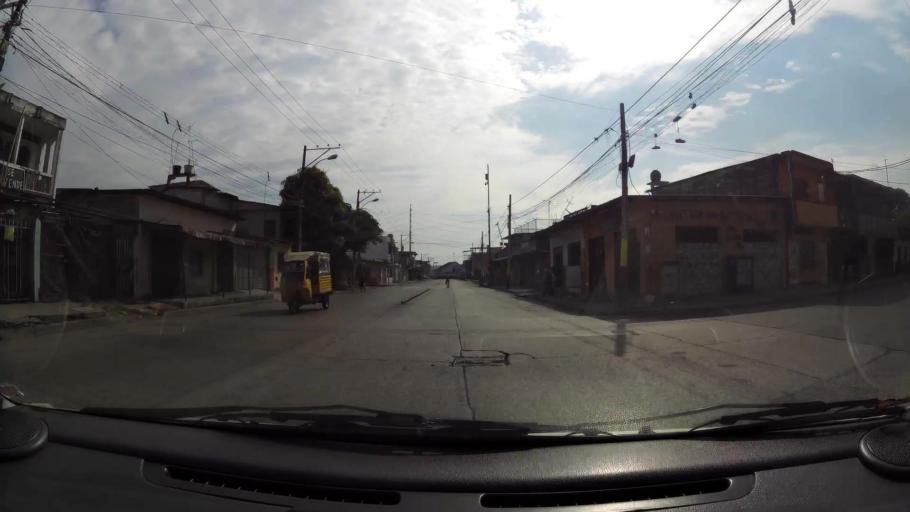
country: EC
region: Guayas
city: Guayaquil
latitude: -2.2546
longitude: -79.9043
